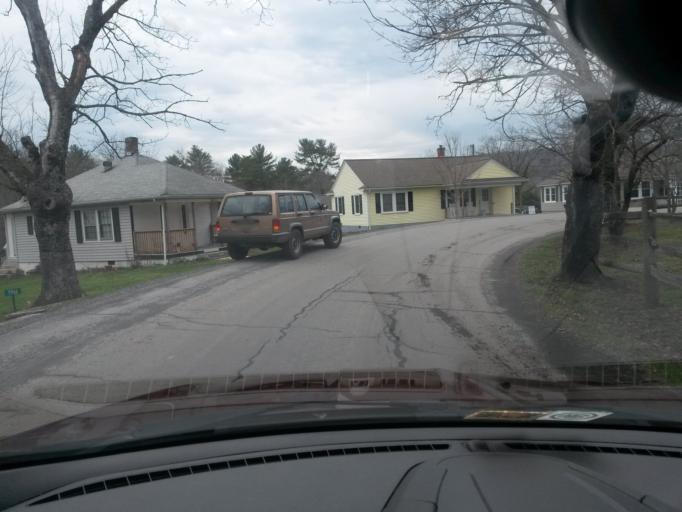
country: US
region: Virginia
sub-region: Bath County
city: Warm Springs
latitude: 38.0536
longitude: -79.8463
